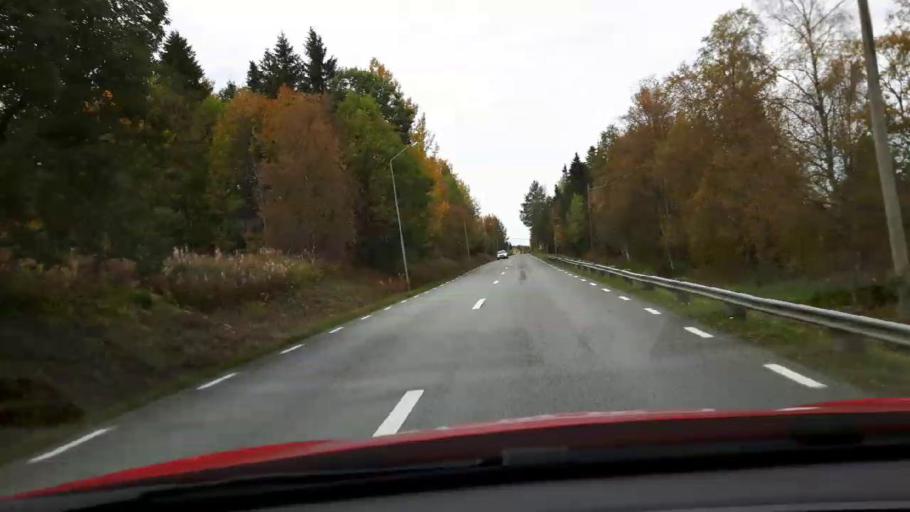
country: SE
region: Jaemtland
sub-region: Krokoms Kommun
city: Krokom
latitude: 63.1832
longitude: 14.0784
